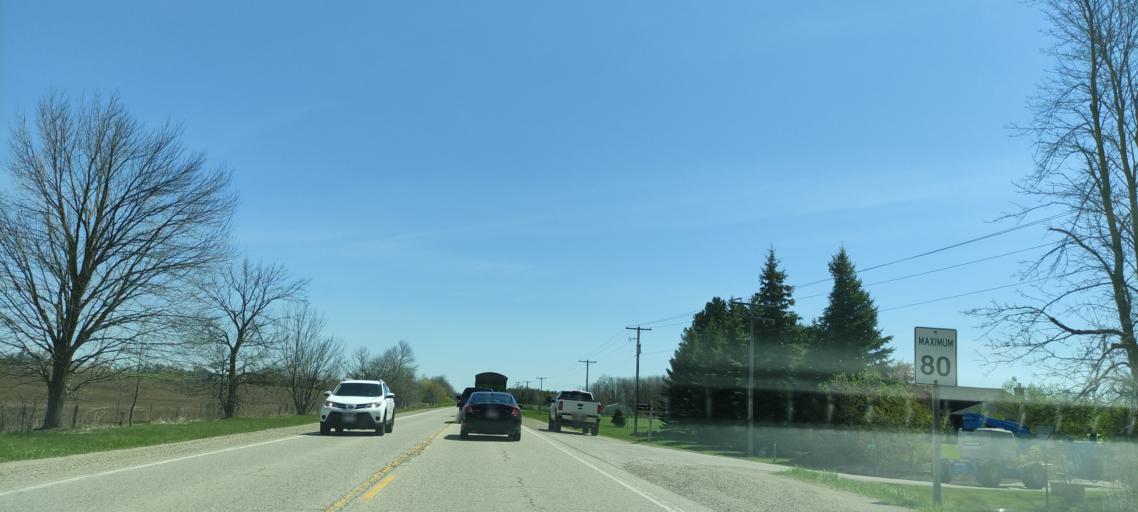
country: CA
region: Ontario
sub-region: Wellington County
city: Guelph
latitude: 43.5741
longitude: -80.3977
